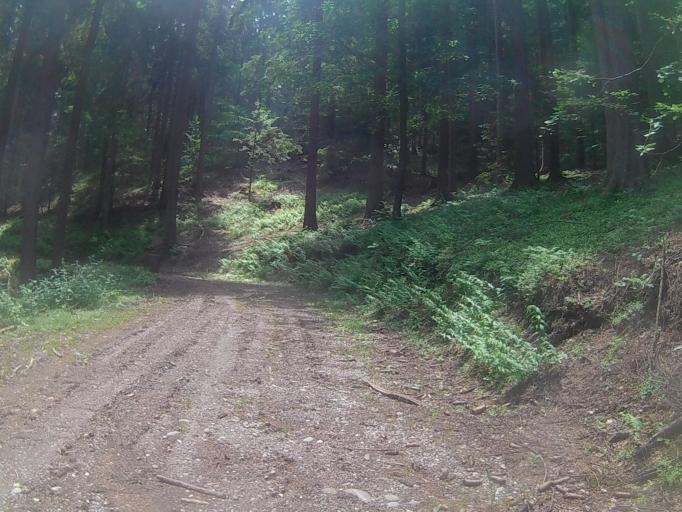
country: SI
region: Ruse
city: Ruse
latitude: 46.5170
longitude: 15.5440
